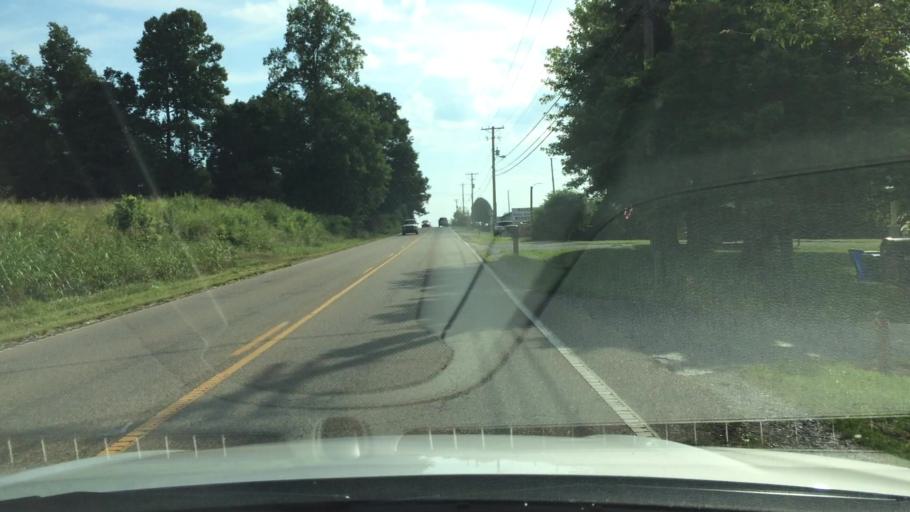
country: US
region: Tennessee
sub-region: Sevier County
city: Seymour
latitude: 35.9044
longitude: -83.6968
